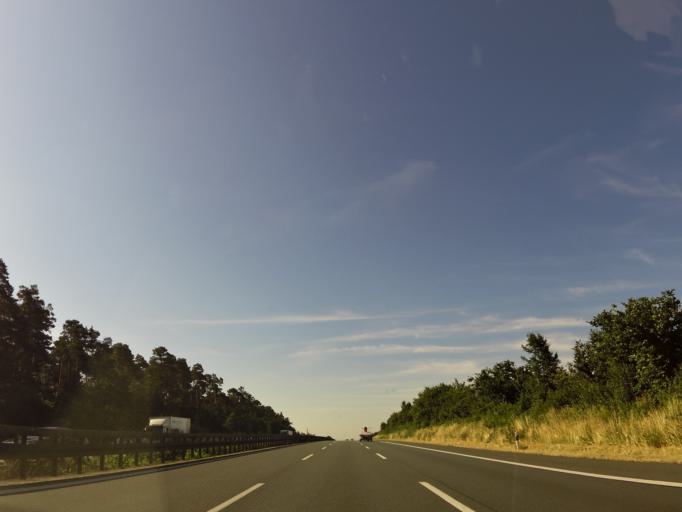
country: DE
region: Bavaria
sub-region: Regierungsbezirk Mittelfranken
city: Allersberg
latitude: 49.2700
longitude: 11.2113
